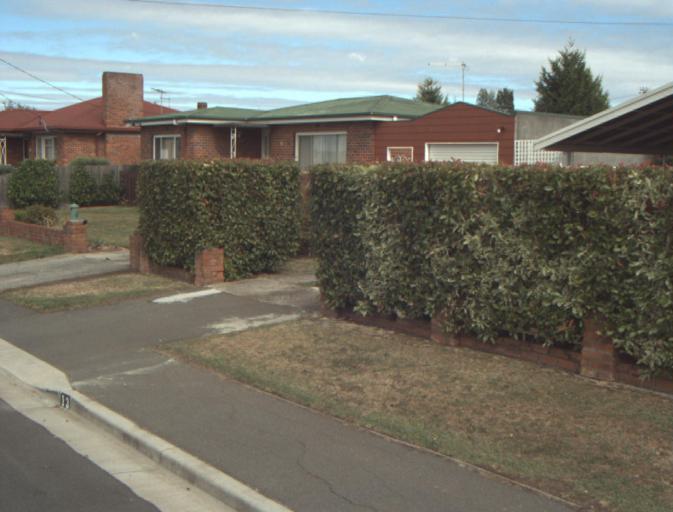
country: AU
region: Tasmania
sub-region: Launceston
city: Mayfield
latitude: -41.3788
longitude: 147.1293
